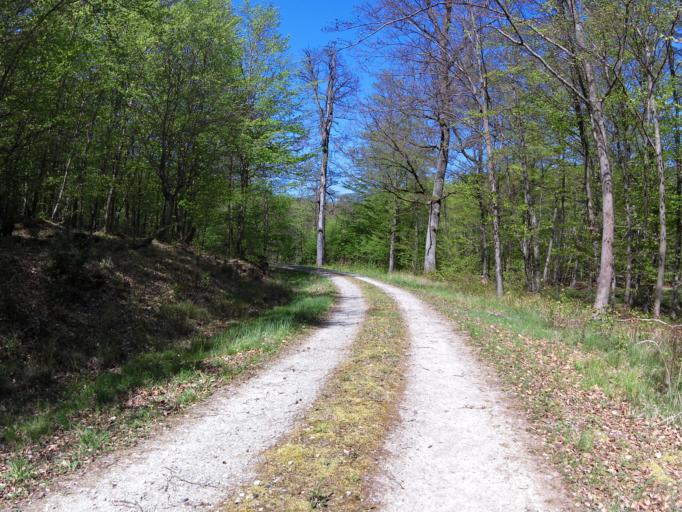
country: DE
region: Thuringia
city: Krauthausen
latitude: 50.9789
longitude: 10.2374
